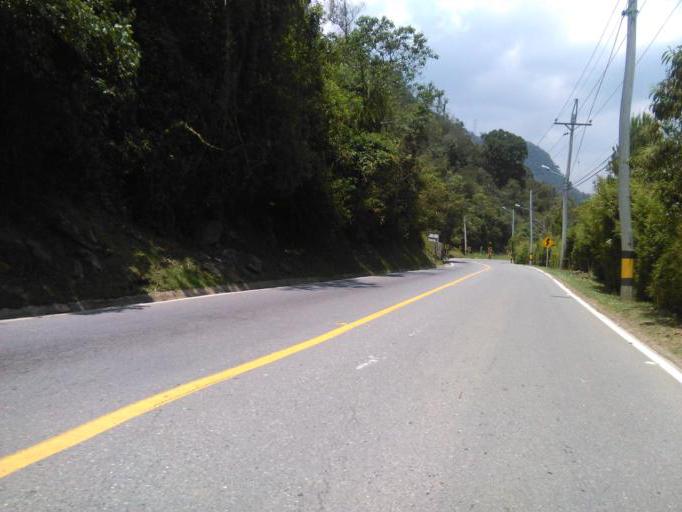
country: CO
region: Antioquia
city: La Union
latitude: 6.0024
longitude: -75.3850
